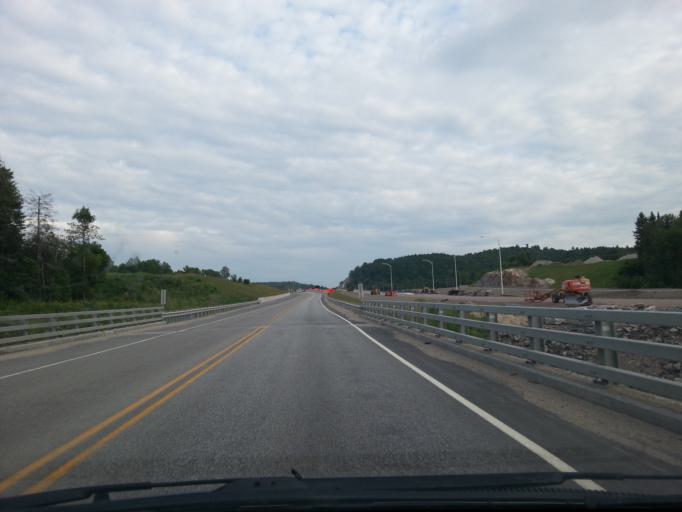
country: CA
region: Quebec
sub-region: Outaouais
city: Wakefield
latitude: 45.6324
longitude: -75.9398
